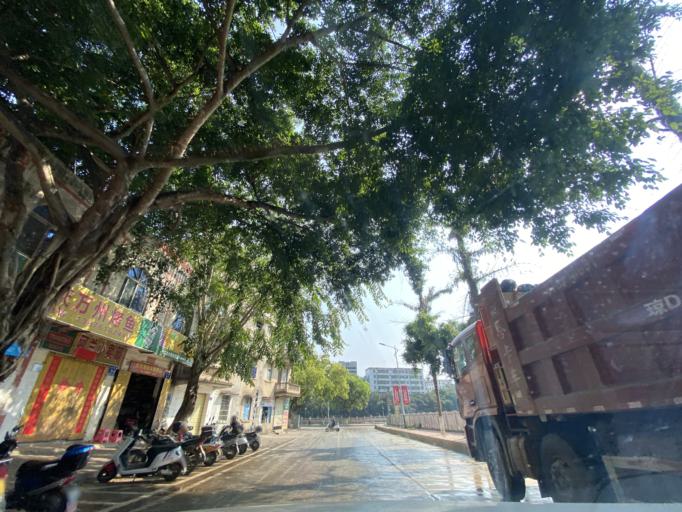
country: CN
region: Hainan
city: Chongshan
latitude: 18.7827
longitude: 109.5137
